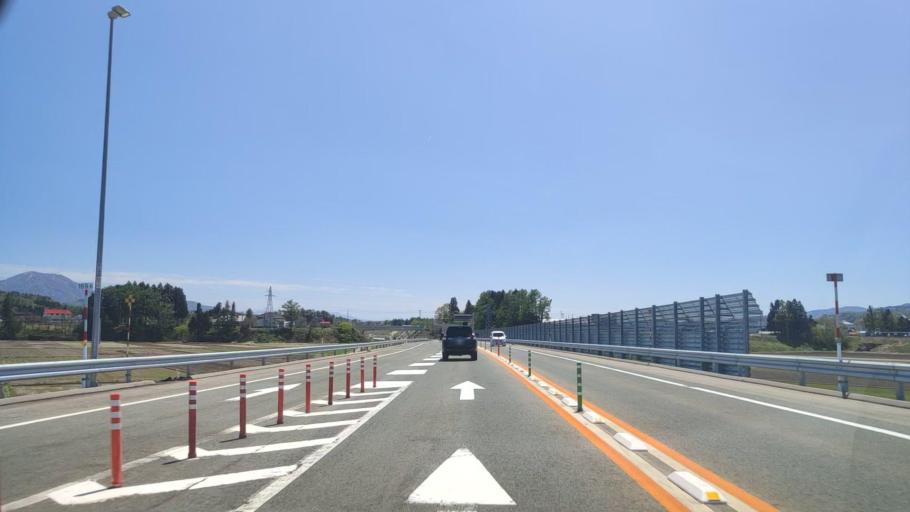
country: JP
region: Yamagata
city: Obanazawa
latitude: 38.6021
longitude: 140.3869
